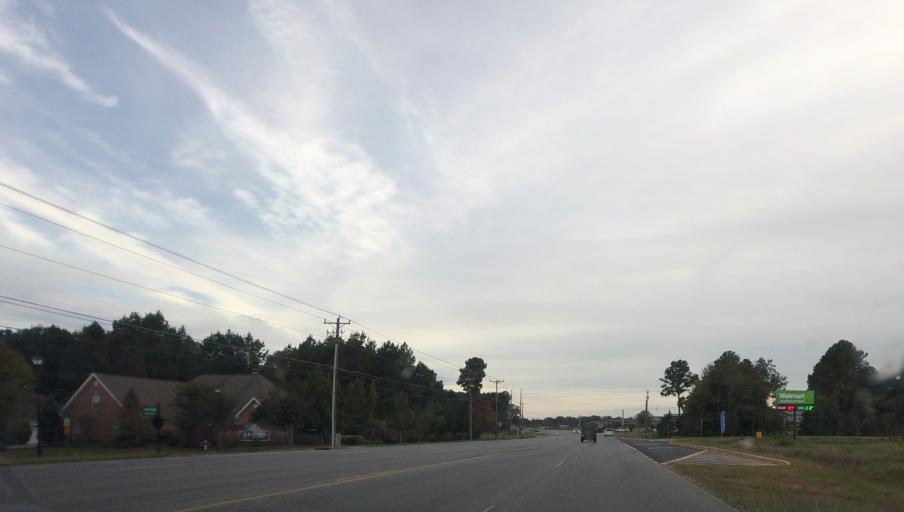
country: US
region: Georgia
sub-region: Houston County
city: Centerville
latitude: 32.5799
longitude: -83.6937
